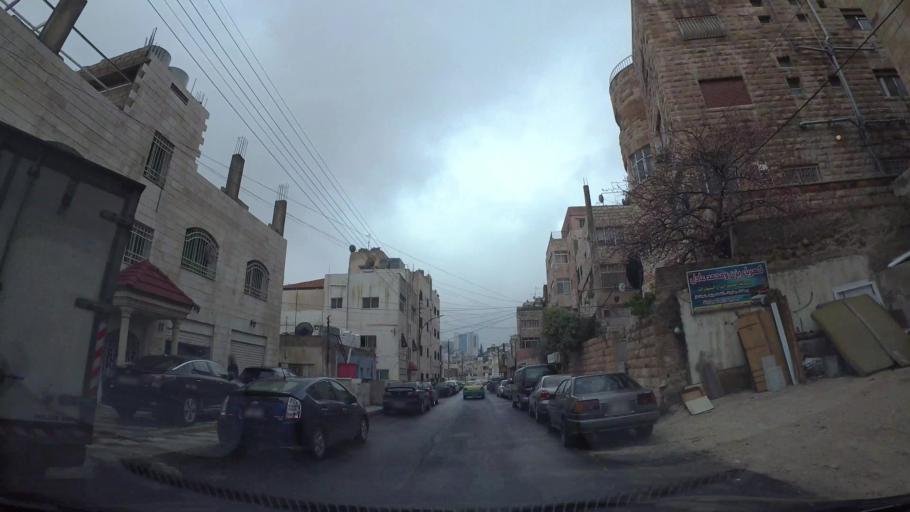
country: JO
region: Amman
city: Amman
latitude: 31.9508
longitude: 35.9144
